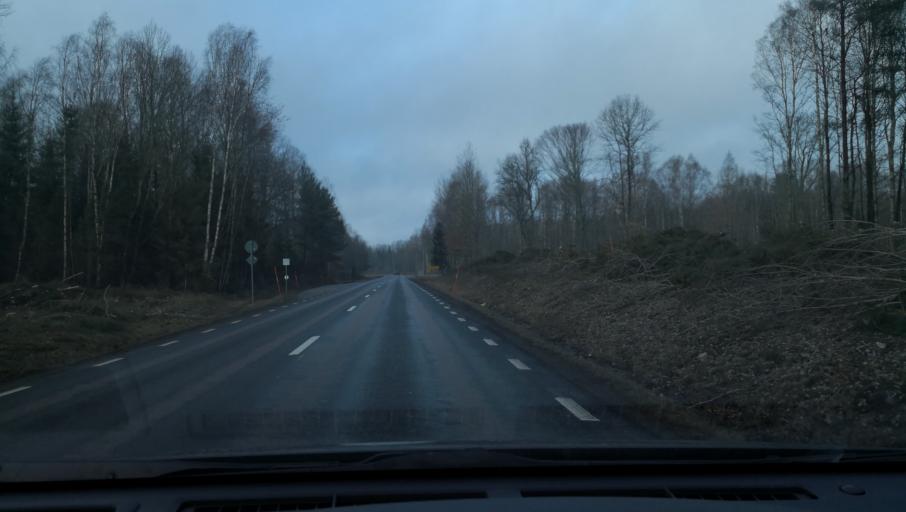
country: SE
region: Vaestra Goetaland
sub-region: Gullspangs Kommun
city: Gullspang
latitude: 58.9499
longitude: 14.0773
